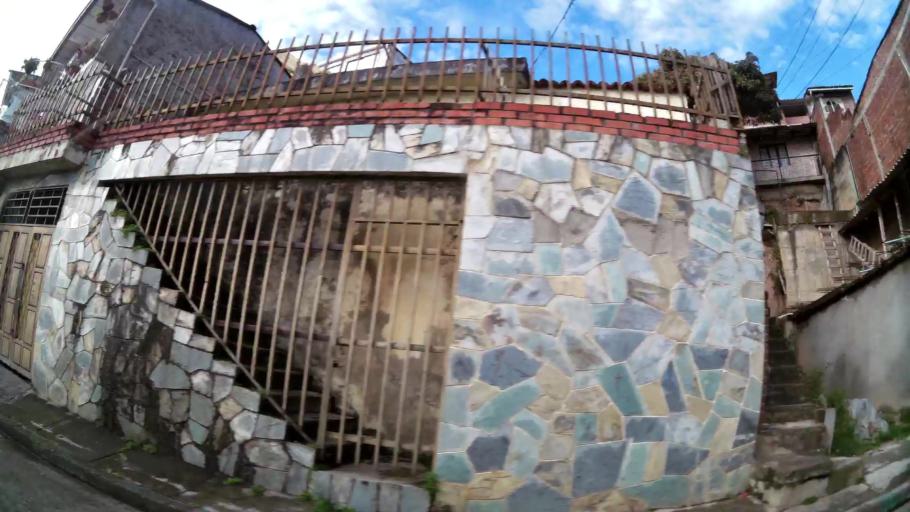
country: CO
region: Valle del Cauca
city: Cali
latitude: 3.4420
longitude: -76.5499
